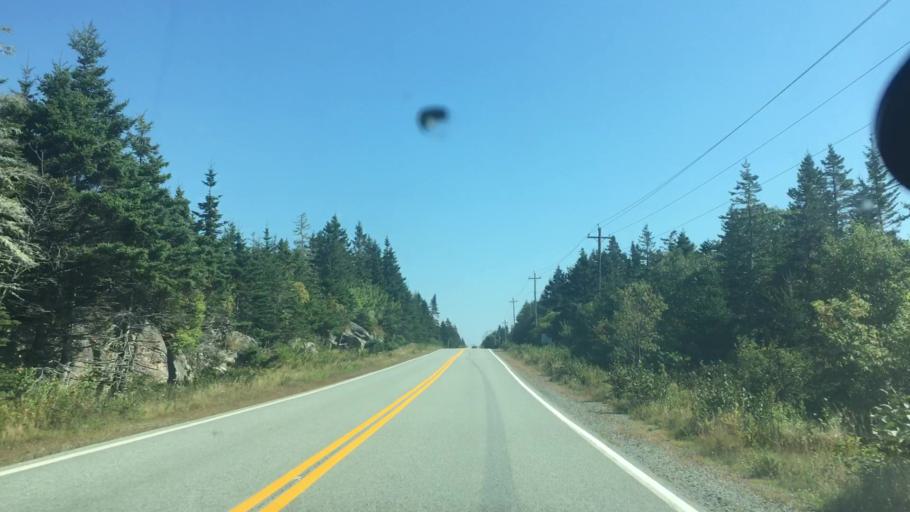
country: CA
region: Nova Scotia
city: New Glasgow
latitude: 44.9314
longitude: -62.2931
